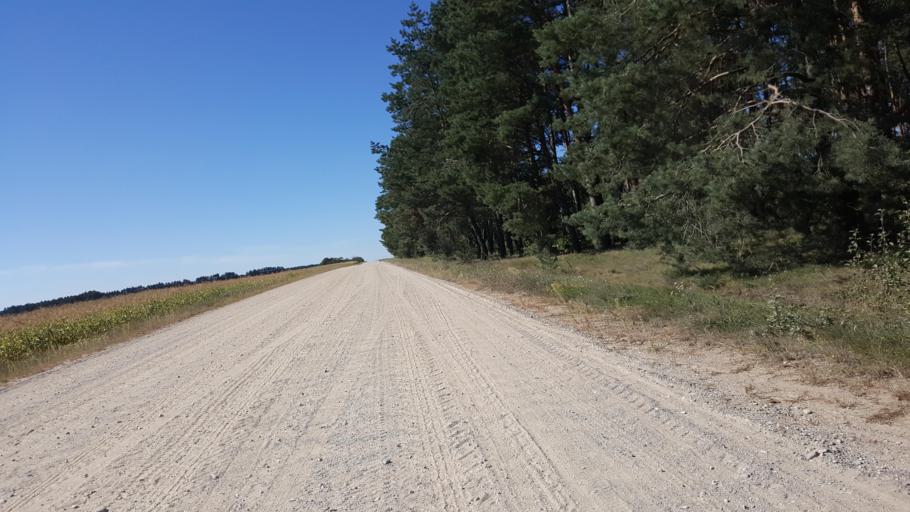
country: PL
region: Lublin Voivodeship
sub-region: Powiat bialski
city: Rokitno
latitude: 52.2264
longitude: 23.3349
